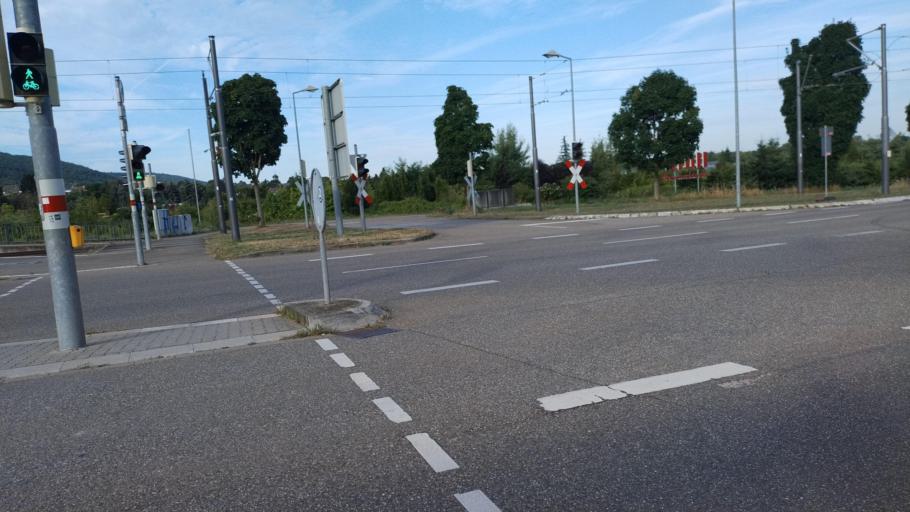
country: DE
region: Baden-Wuerttemberg
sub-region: Karlsruhe Region
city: Karlsruhe
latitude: 48.9831
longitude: 8.4602
